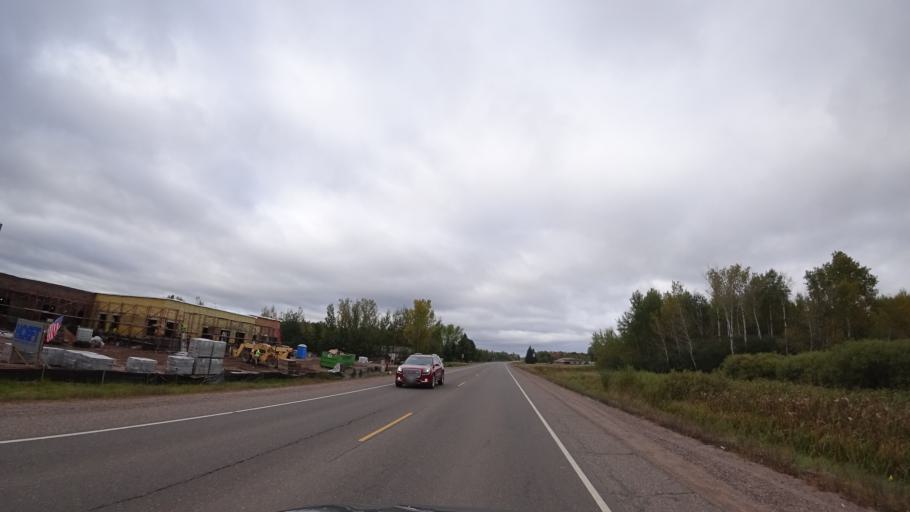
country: US
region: Wisconsin
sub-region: Rusk County
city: Ladysmith
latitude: 45.4771
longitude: -91.1112
